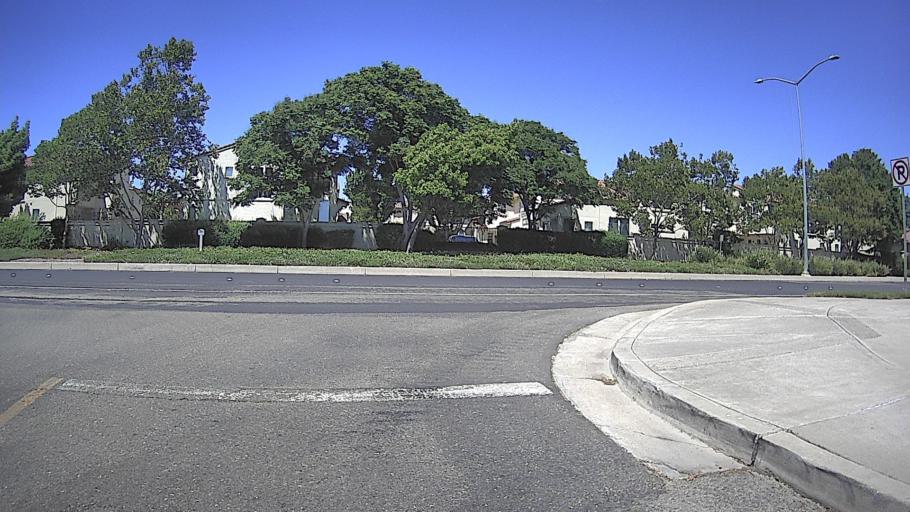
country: US
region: California
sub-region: Alameda County
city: Pleasanton
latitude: 37.7123
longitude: -121.8737
